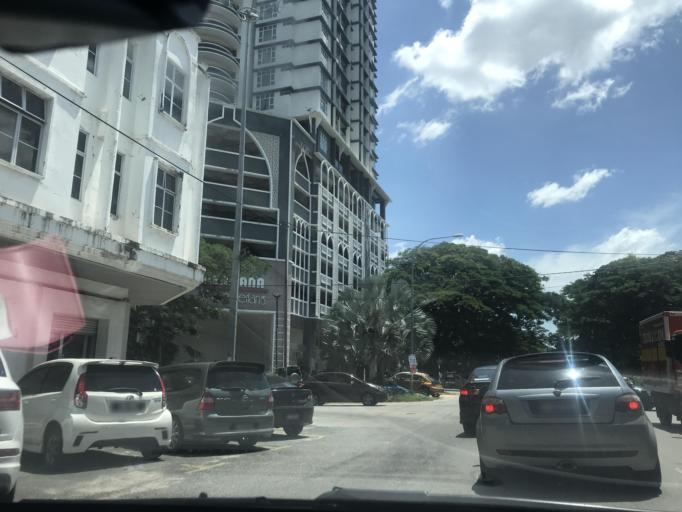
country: MY
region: Kelantan
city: Kota Bharu
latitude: 6.1293
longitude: 102.2474
